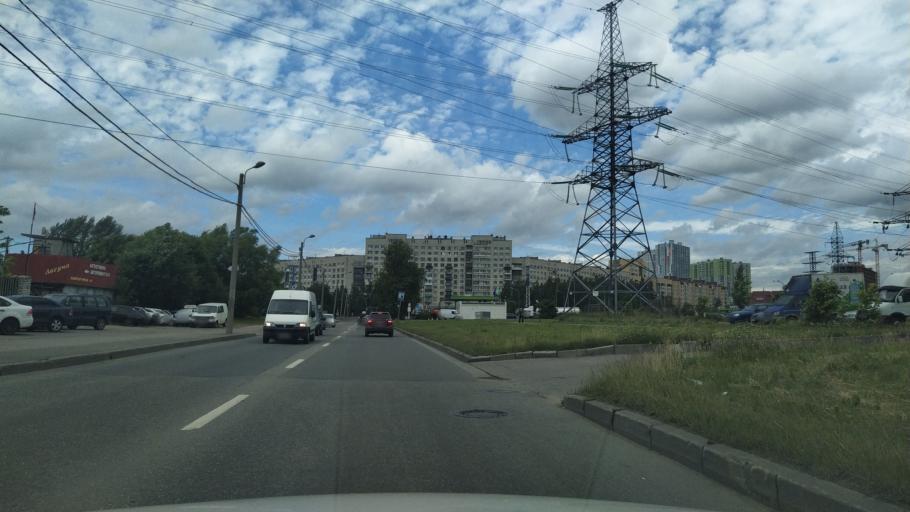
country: RU
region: Leningrad
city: Kalininskiy
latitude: 59.9773
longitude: 30.3829
